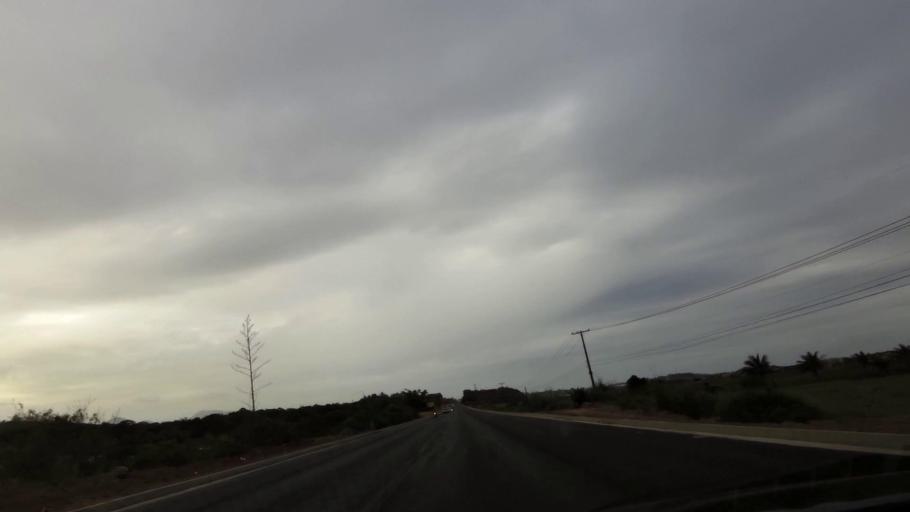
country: BR
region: Espirito Santo
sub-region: Guarapari
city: Guarapari
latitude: -20.7564
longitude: -40.5648
